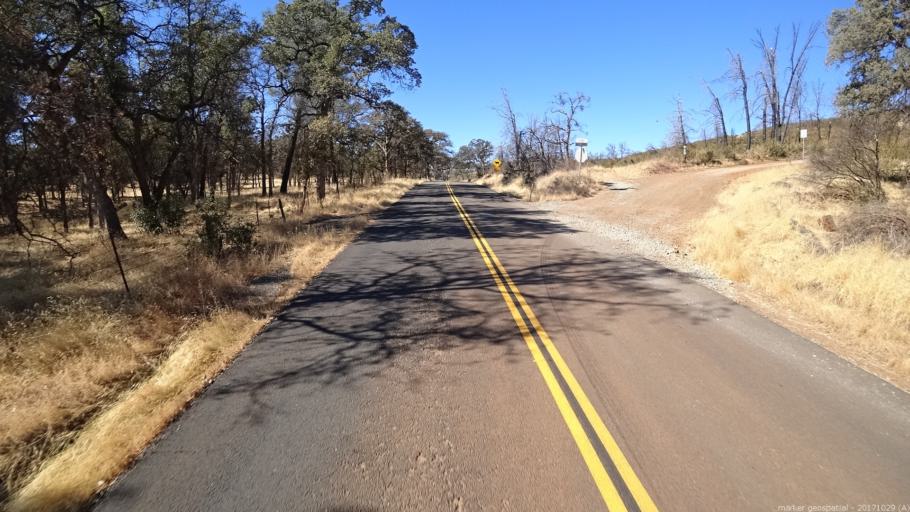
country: US
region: California
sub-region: Trinity County
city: Lewiston
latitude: 40.4240
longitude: -122.7614
